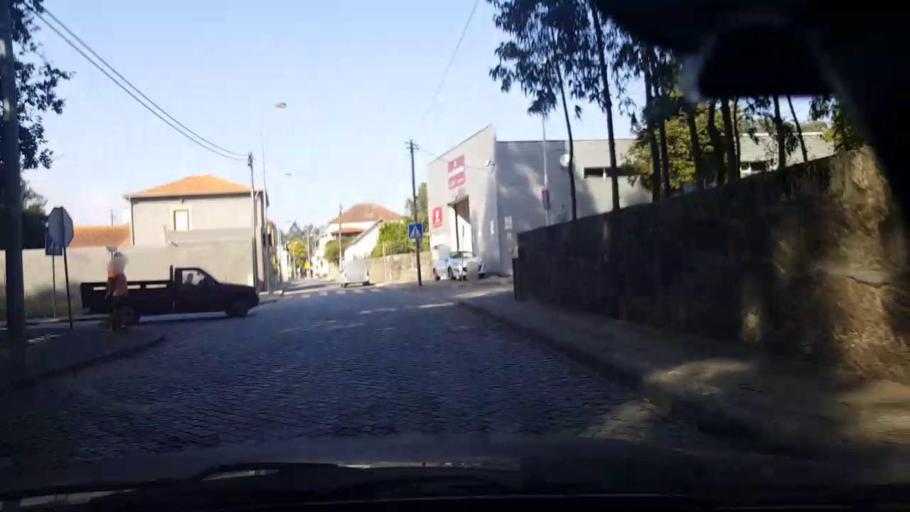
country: PT
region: Porto
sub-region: Maia
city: Gemunde
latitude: 41.2692
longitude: -8.6807
